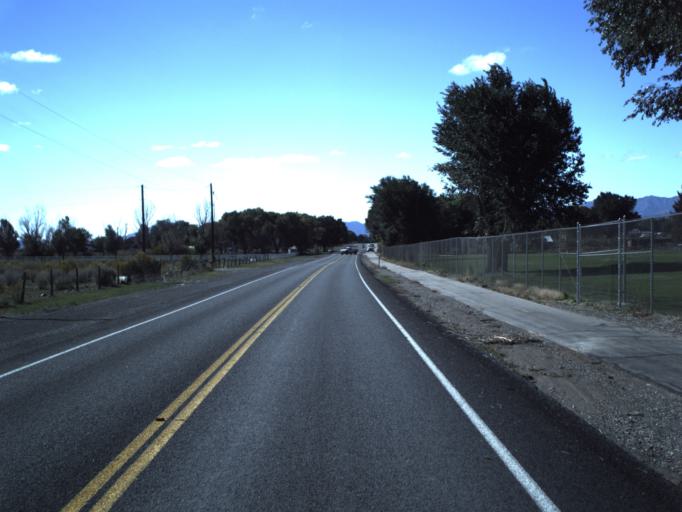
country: US
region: Utah
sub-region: Beaver County
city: Beaver
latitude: 38.2767
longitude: -112.6083
